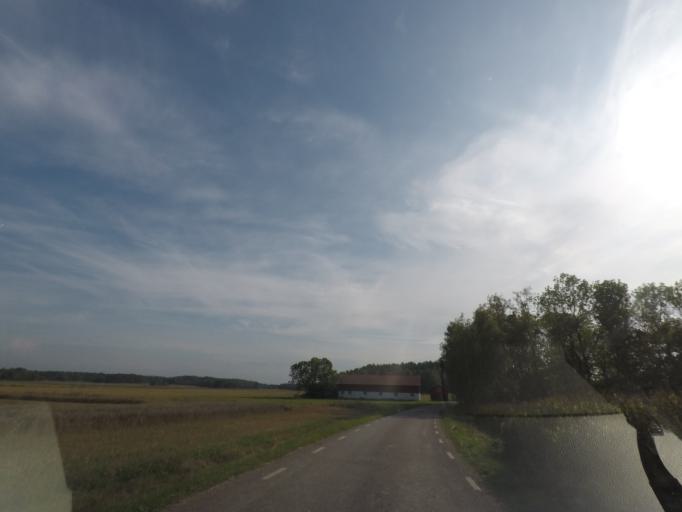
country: SE
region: Vaestmanland
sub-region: Kungsors Kommun
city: Kungsoer
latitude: 59.5035
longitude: 16.1556
